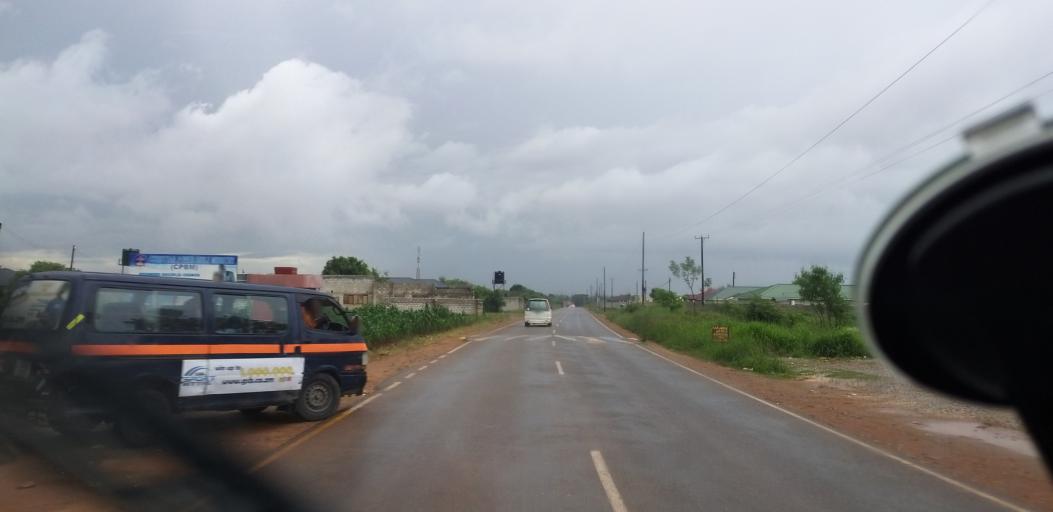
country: ZM
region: Lusaka
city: Lusaka
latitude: -15.4953
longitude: 28.3129
